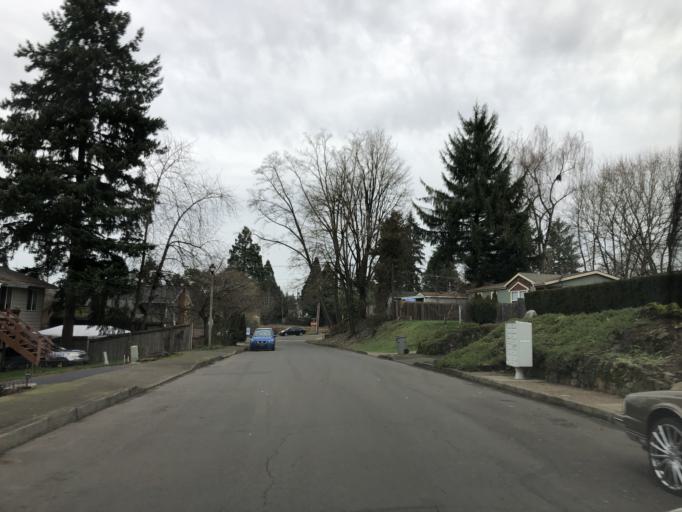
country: US
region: Oregon
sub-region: Washington County
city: Tigard
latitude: 45.4288
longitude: -122.7847
